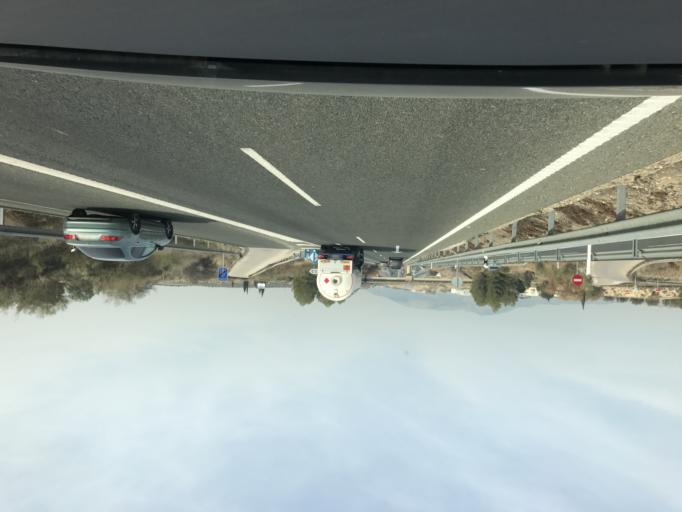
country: ES
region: Andalusia
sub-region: Provincia de Granada
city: Huetor-Tajar
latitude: 37.1886
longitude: -4.0288
